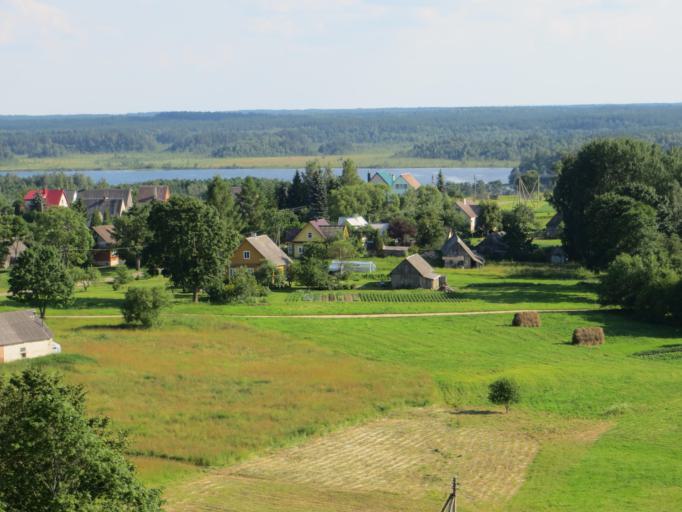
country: LT
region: Utenos apskritis
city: Visaginas
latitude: 55.6434
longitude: 26.3587
